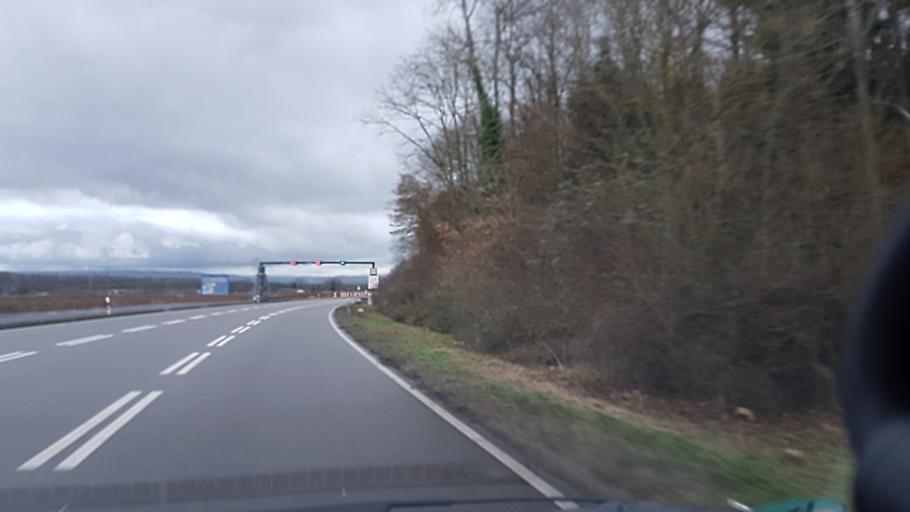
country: DE
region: Baden-Wuerttemberg
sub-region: Freiburg Region
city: Rust
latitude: 48.2592
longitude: 7.7346
